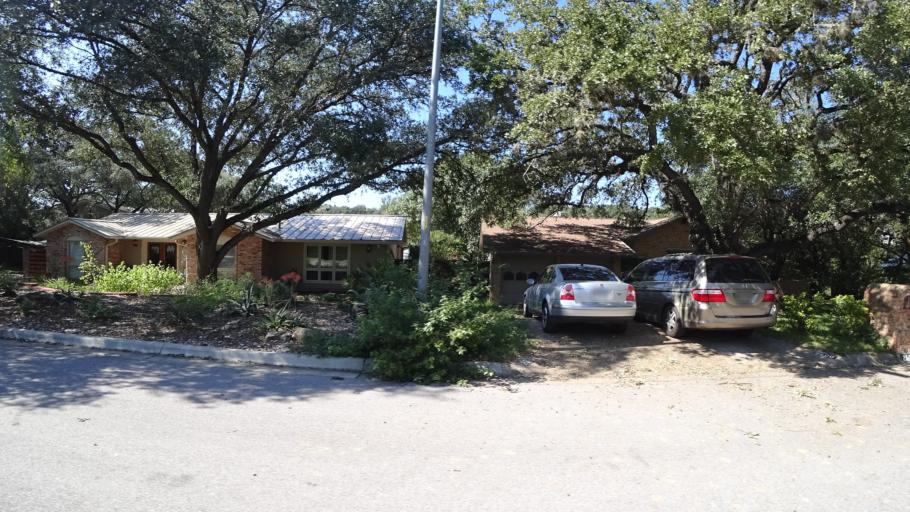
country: US
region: Texas
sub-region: Travis County
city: Rollingwood
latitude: 30.2533
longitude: -97.7928
